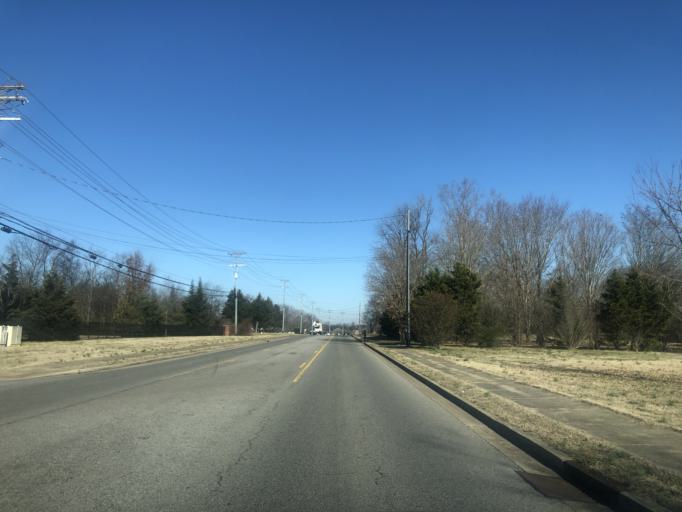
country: US
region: Tennessee
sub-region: Rutherford County
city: Smyrna
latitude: 35.9097
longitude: -86.4724
